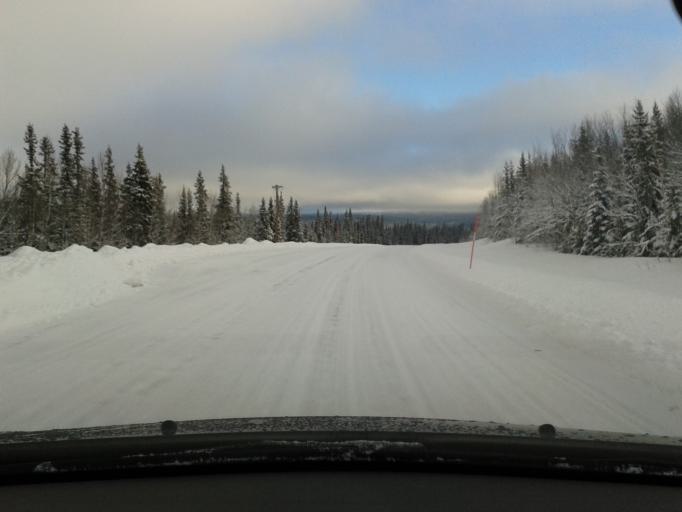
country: SE
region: Vaesterbotten
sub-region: Vilhelmina Kommun
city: Sjoberg
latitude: 65.2557
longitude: 15.6475
